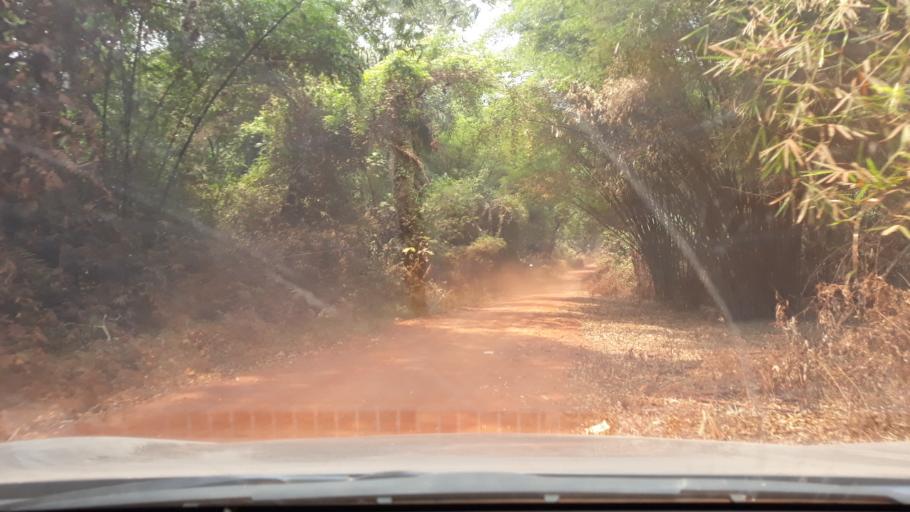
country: CD
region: Eastern Province
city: Buta
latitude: 2.3746
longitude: 24.9241
